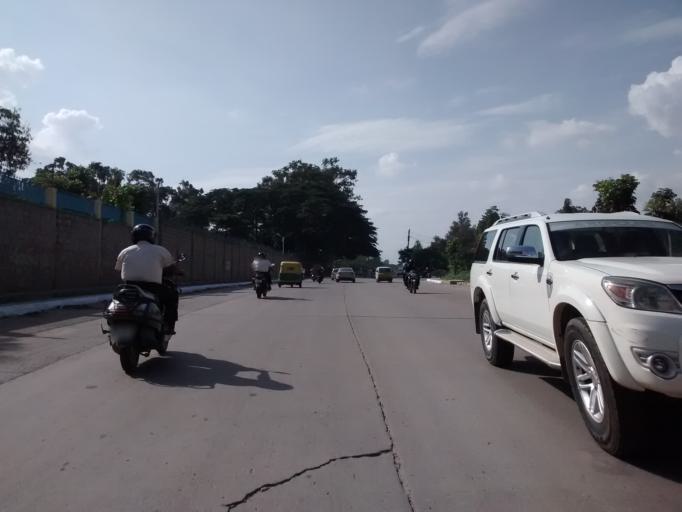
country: IN
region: Karnataka
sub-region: Bangalore Urban
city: Bangalore
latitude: 12.9807
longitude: 77.6512
